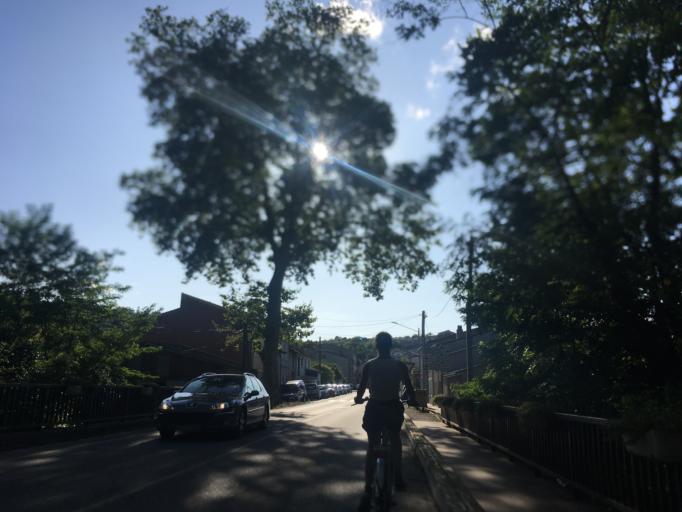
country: FR
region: Midi-Pyrenees
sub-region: Departement de la Haute-Garonne
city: Gardouch
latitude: 43.3904
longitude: 1.6862
